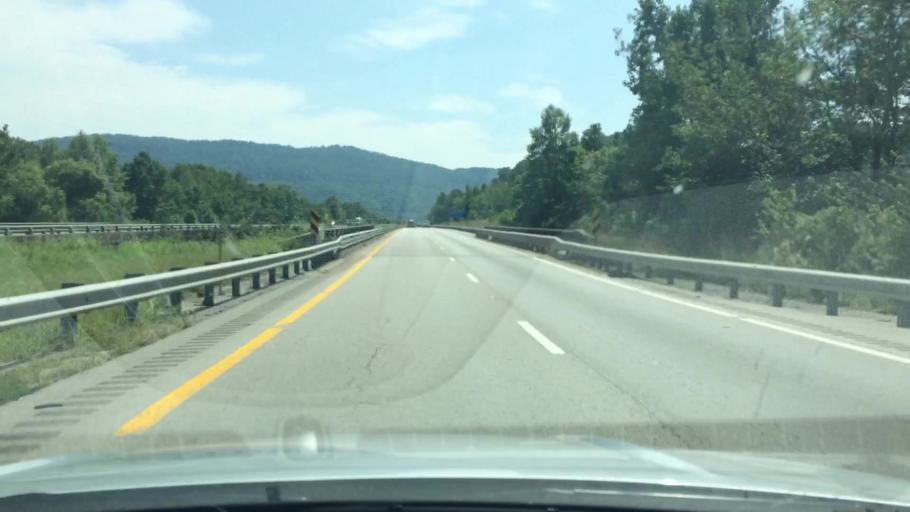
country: US
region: Tennessee
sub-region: Campbell County
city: Jellico
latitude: 36.6065
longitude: -84.1061
